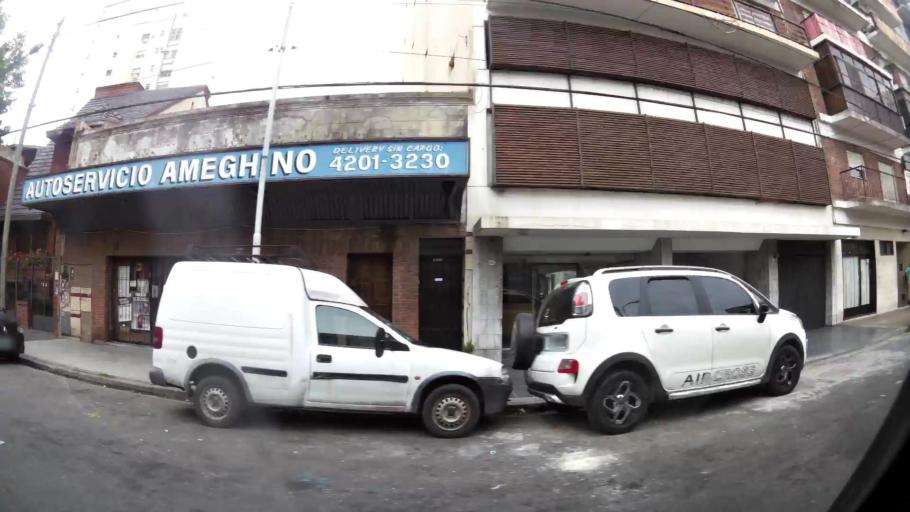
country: AR
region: Buenos Aires
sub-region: Partido de Avellaneda
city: Avellaneda
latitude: -34.6636
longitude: -58.3611
